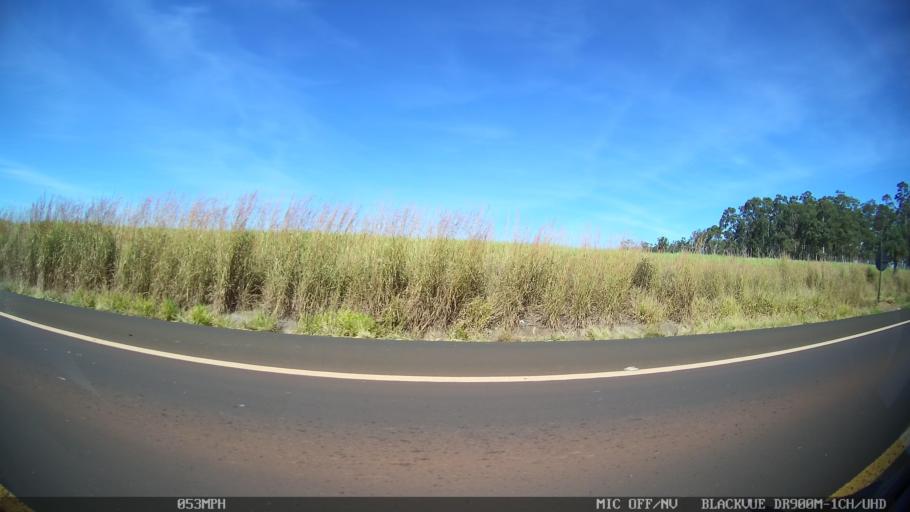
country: BR
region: Sao Paulo
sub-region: Franca
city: Franca
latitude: -20.5616
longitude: -47.5088
